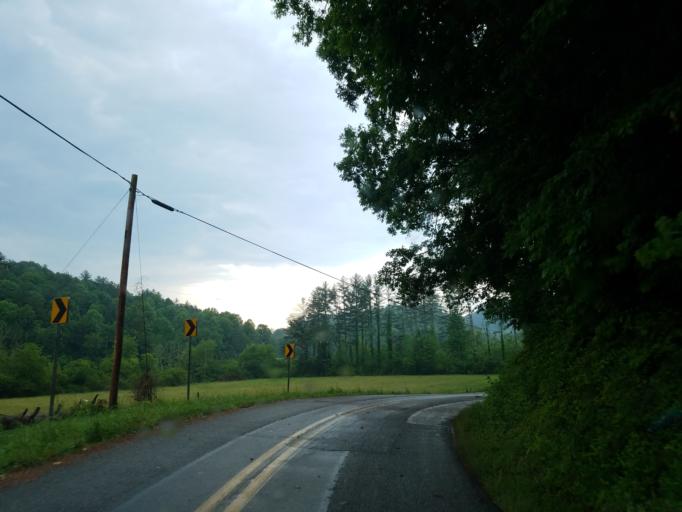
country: US
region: Georgia
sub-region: Lumpkin County
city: Dahlonega
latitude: 34.7068
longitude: -84.0766
